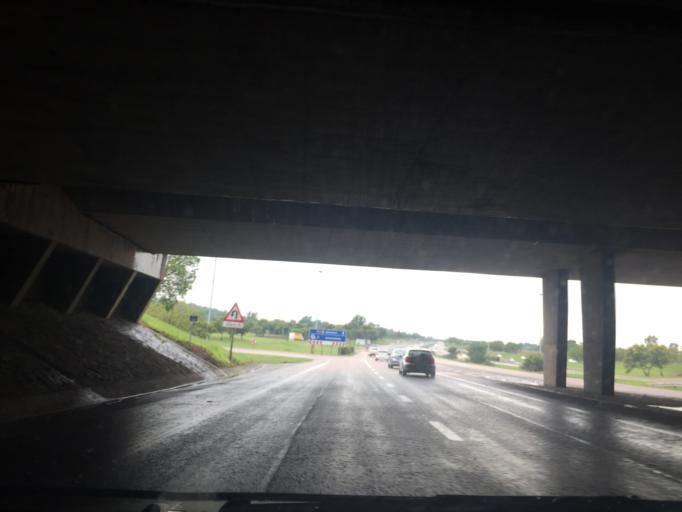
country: ZA
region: Gauteng
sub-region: City of Tshwane Metropolitan Municipality
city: Pretoria
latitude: -25.7400
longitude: 28.2647
